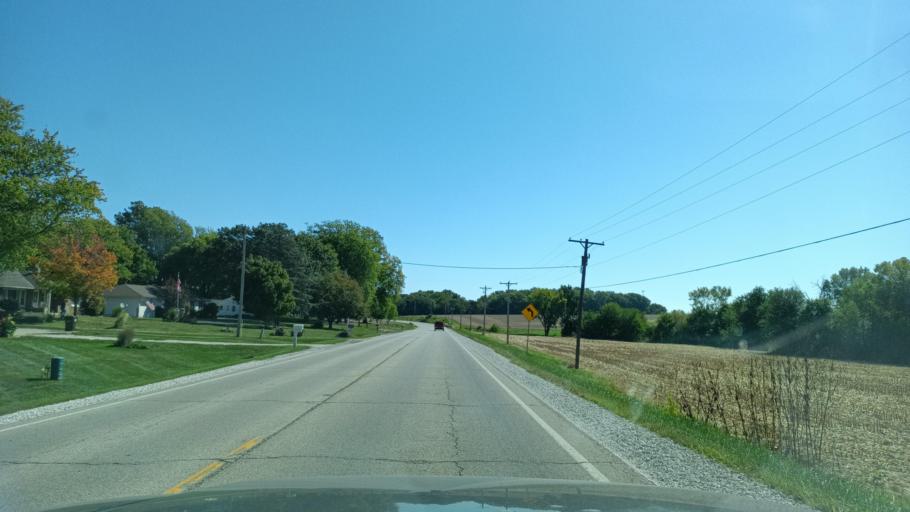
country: US
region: Illinois
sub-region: Peoria County
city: Hanna City
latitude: 40.7910
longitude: -89.7632
